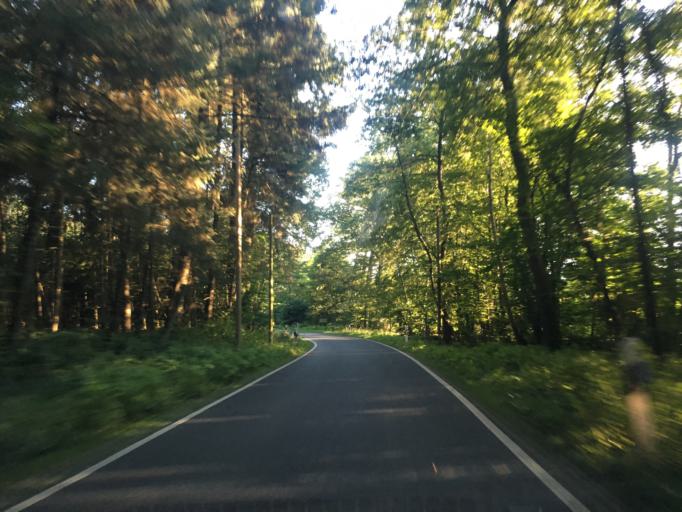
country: DE
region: North Rhine-Westphalia
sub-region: Regierungsbezirk Munster
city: Muenster
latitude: 51.9117
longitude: 7.6092
